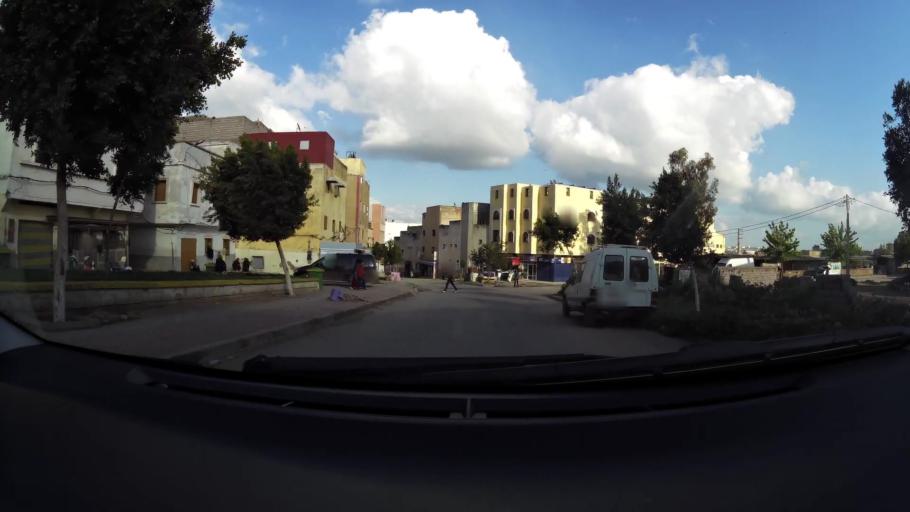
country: MA
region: Chaouia-Ouardigha
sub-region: Settat Province
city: Settat
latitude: 33.0034
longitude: -7.6275
